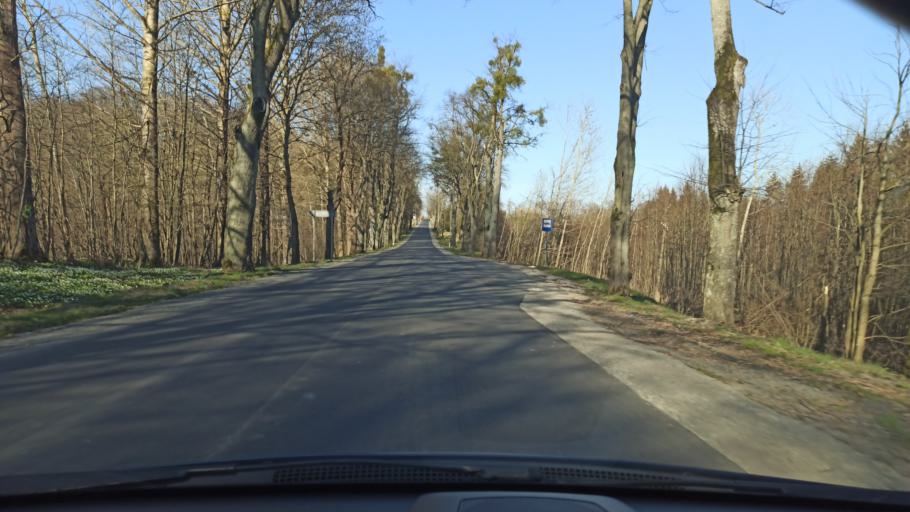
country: PL
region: Warmian-Masurian Voivodeship
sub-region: Powiat elblaski
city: Gronowo Gorne
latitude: 54.2038
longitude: 19.4989
